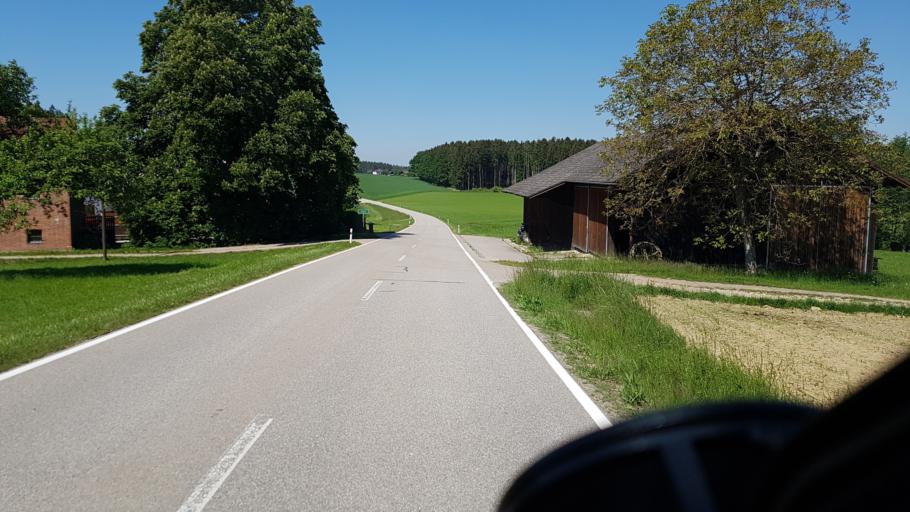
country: DE
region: Bavaria
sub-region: Lower Bavaria
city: Reut
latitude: 48.3386
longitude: 12.9397
